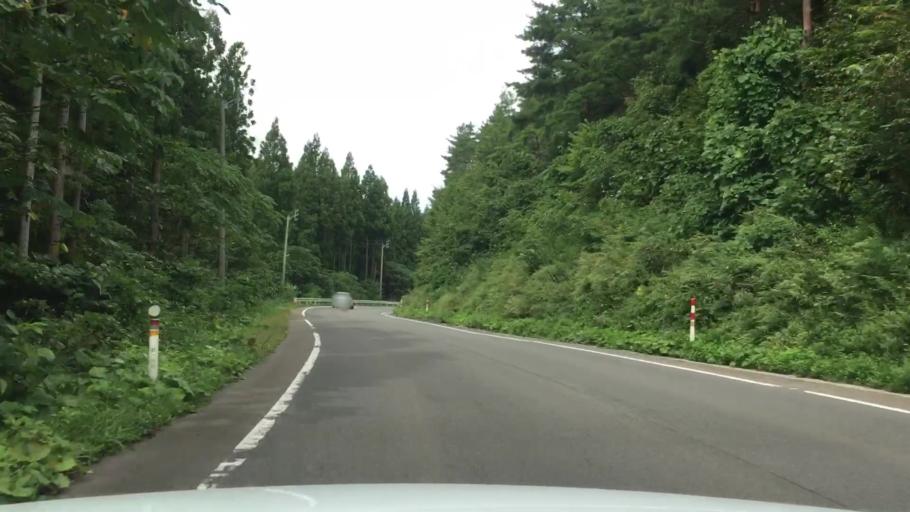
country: JP
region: Aomori
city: Shimokizukuri
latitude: 40.7224
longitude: 140.2581
